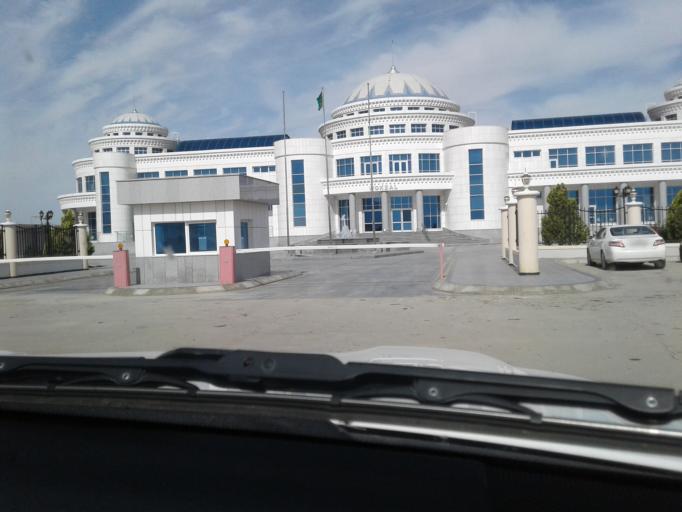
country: TM
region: Balkan
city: Gazanjyk
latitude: 39.2674
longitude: 55.4909
